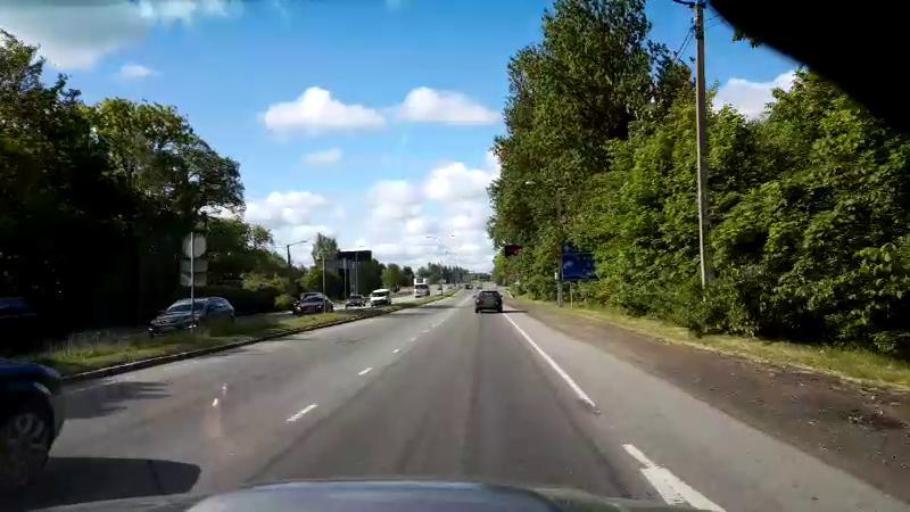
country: EE
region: Harju
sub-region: Saue vald
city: Laagri
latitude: 59.3513
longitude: 24.6279
